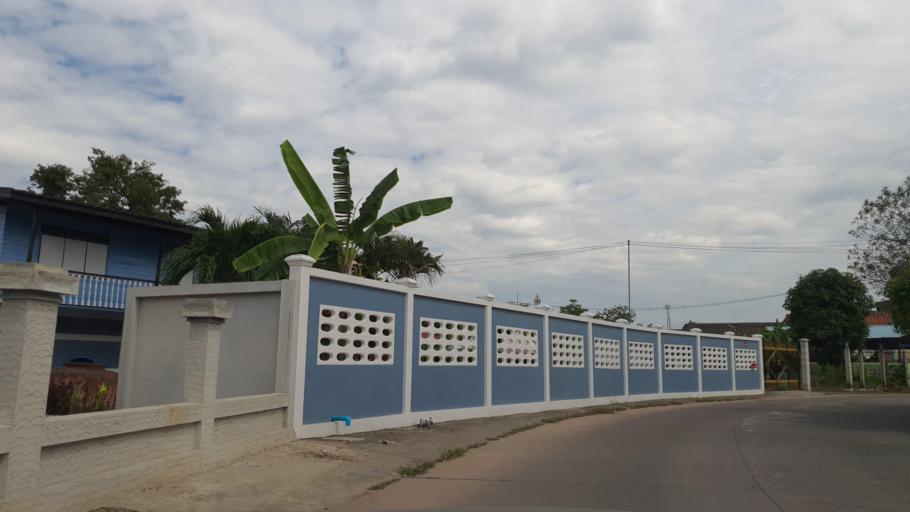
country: TH
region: Chon Buri
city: Phatthaya
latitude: 12.9559
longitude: 100.9182
